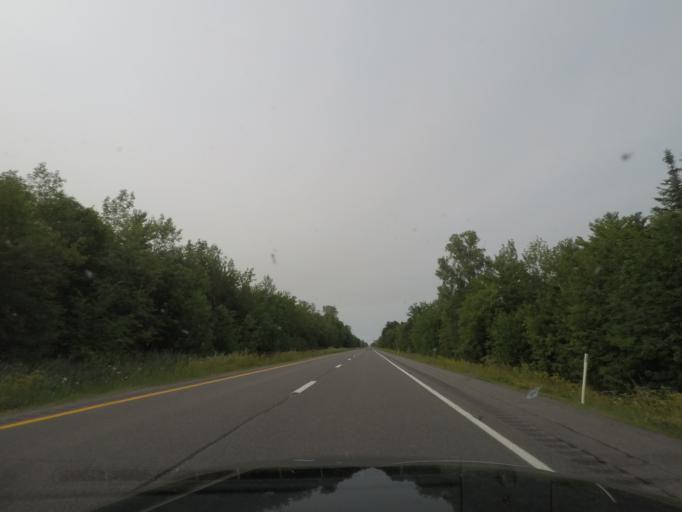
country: US
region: New York
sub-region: Clinton County
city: Champlain
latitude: 44.9330
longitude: -73.4464
